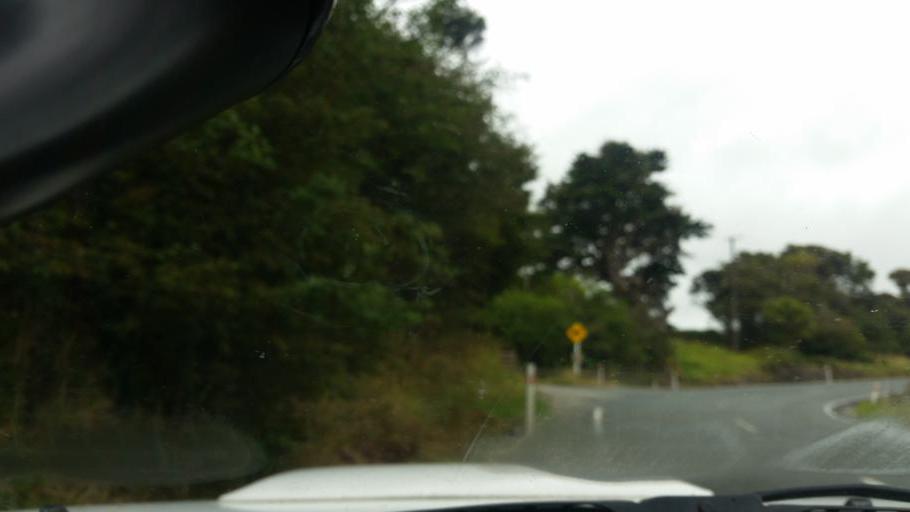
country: NZ
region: Auckland
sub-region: Auckland
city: Wellsford
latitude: -36.1522
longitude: 174.4687
